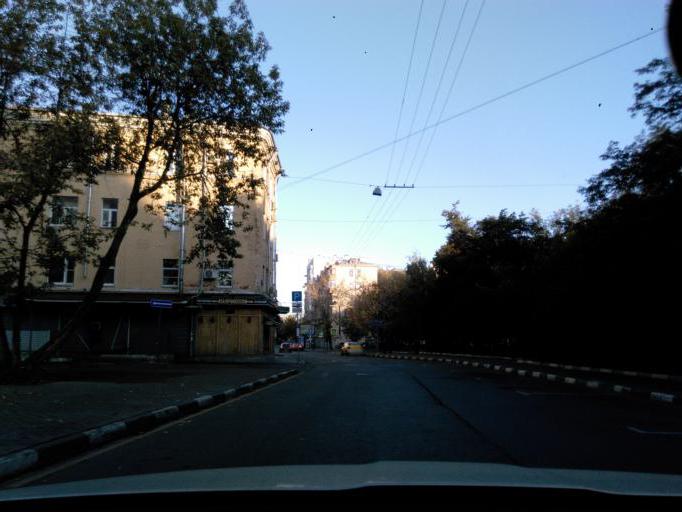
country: RU
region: Moskovskaya
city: Dorogomilovo
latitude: 55.7692
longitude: 37.5858
